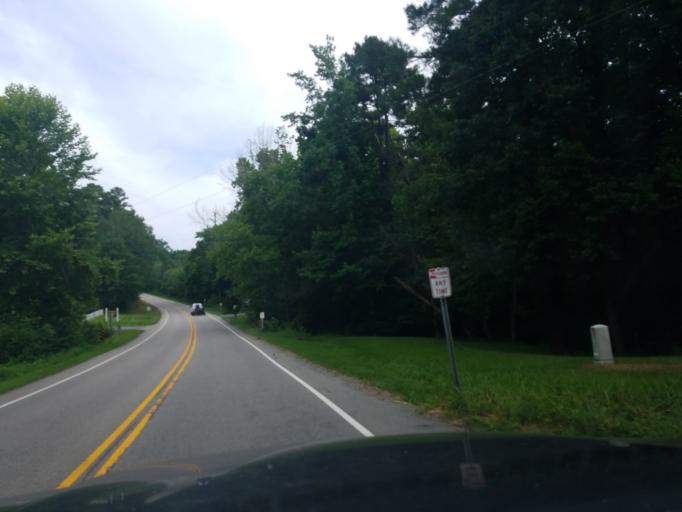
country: US
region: North Carolina
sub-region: Durham County
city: Durham
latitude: 36.1356
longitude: -78.9478
